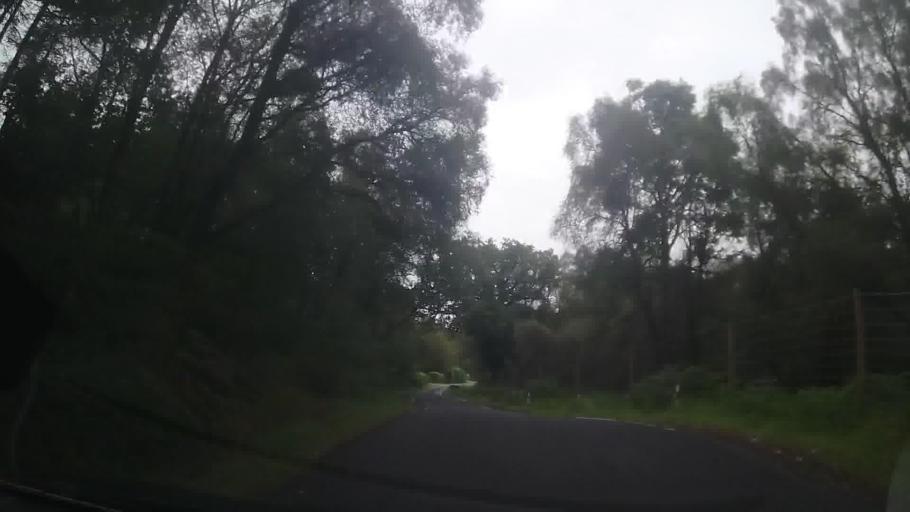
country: GB
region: Scotland
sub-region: Argyll and Bute
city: Isle Of Mull
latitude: 56.7075
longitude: -5.7820
